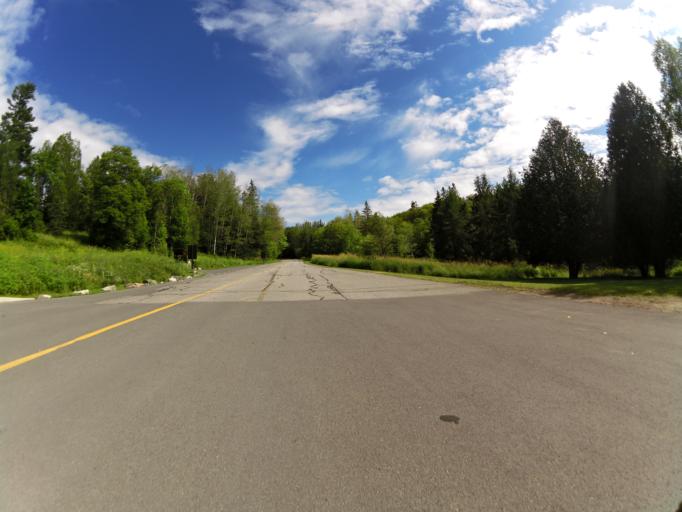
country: CA
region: Quebec
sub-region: Outaouais
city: Wakefield
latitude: 45.6267
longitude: -76.0137
